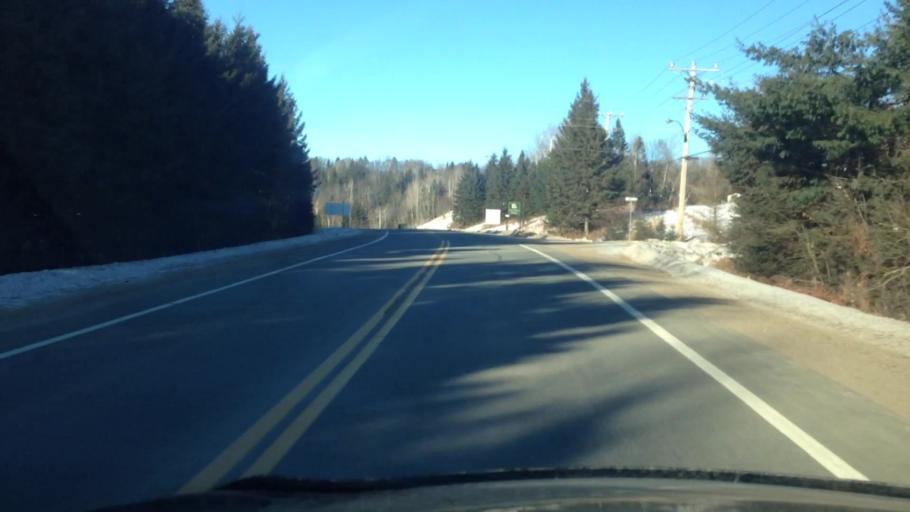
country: CA
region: Quebec
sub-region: Laurentides
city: Mont-Tremblant
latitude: 46.0484
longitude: -74.6088
